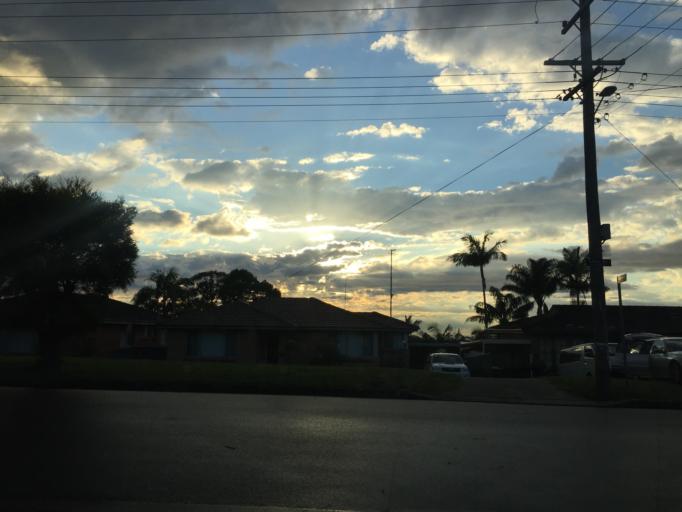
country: AU
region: New South Wales
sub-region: Shellharbour
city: Barrack Heights
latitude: -34.5636
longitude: 150.8467
